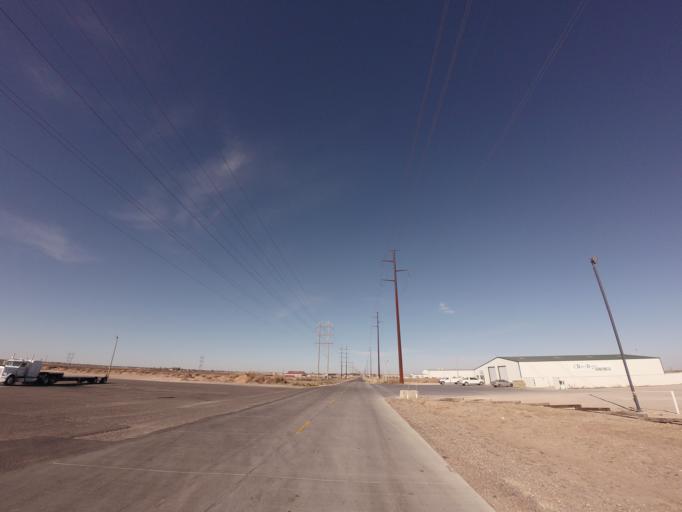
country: US
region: New Mexico
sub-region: Curry County
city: Clovis
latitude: 34.3950
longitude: -103.1433
